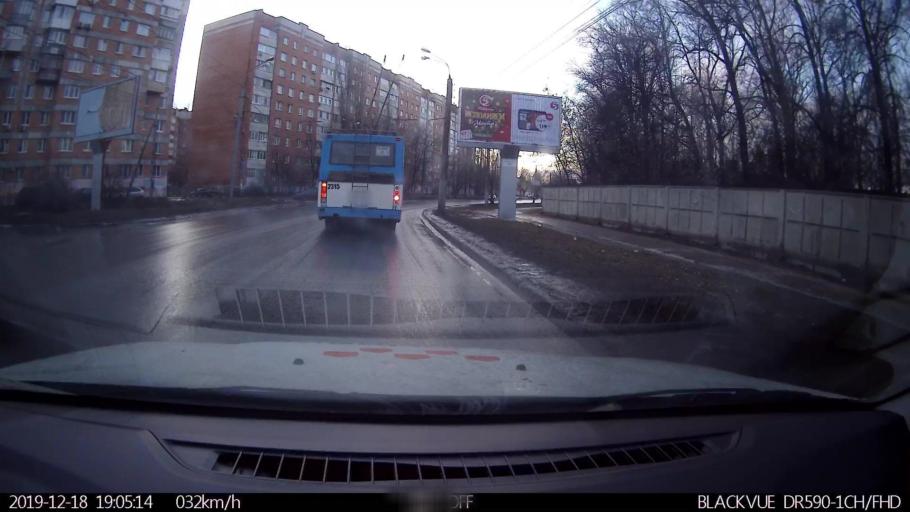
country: RU
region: Nizjnij Novgorod
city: Nizhniy Novgorod
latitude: 56.3282
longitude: 43.8681
